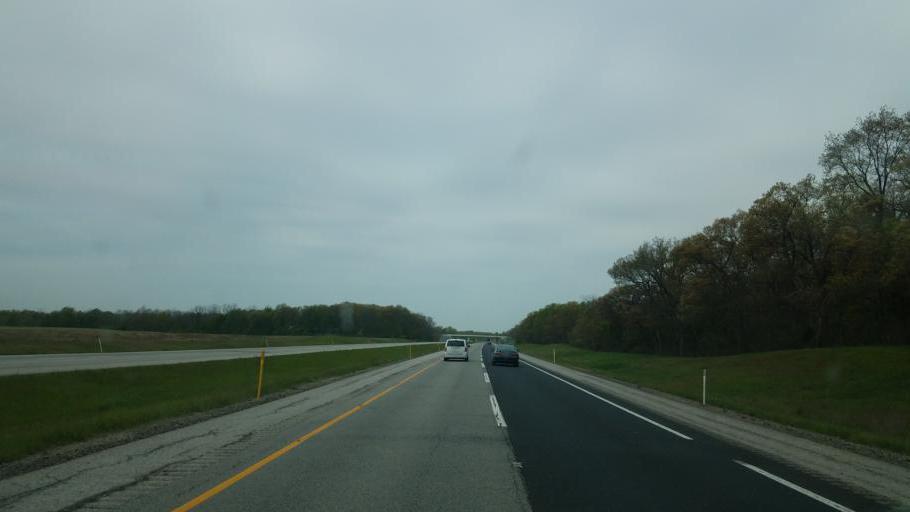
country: US
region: Indiana
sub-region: Elkhart County
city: Bristol
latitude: 41.7331
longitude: -85.7521
